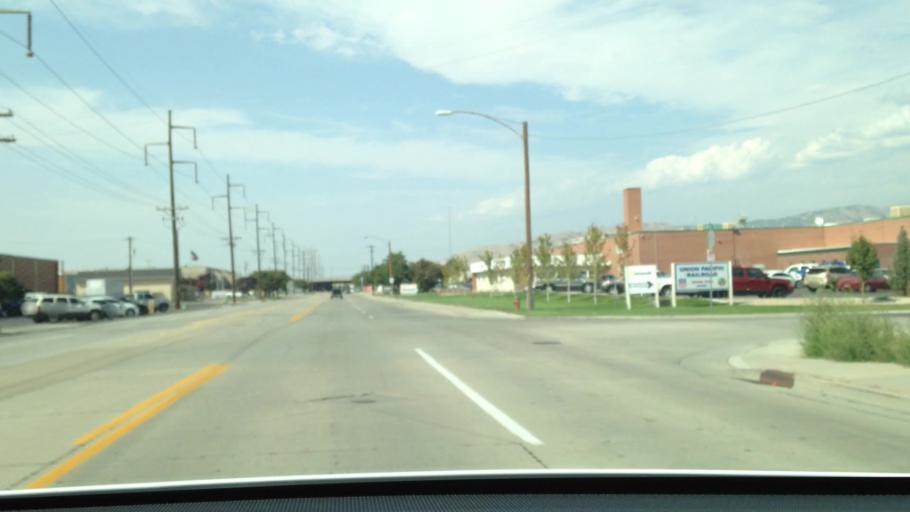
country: US
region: Utah
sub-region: Salt Lake County
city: South Salt Lake
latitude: 40.7182
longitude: -111.9174
